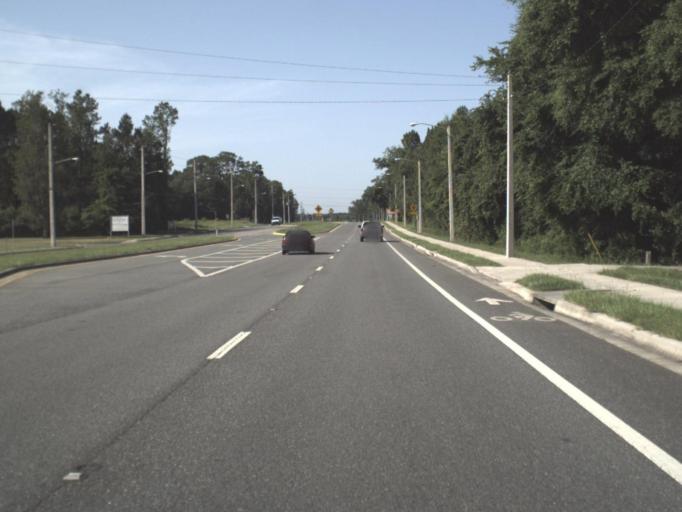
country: US
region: Florida
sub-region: Columbia County
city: Lake City
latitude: 30.1296
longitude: -82.6525
